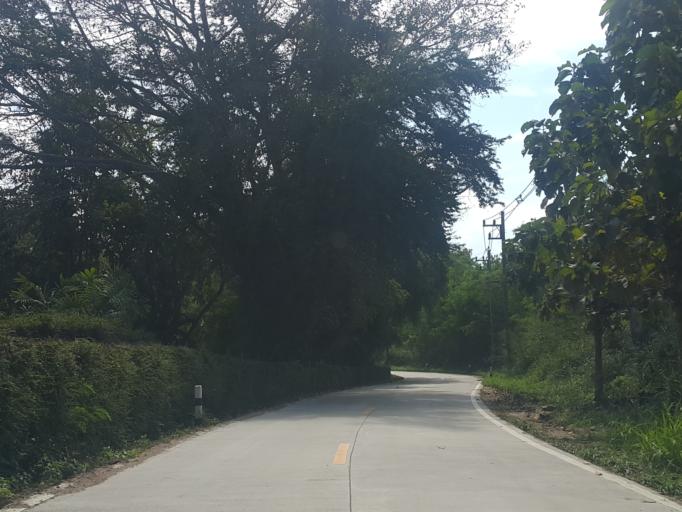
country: TH
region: Chiang Mai
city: Mae On
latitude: 18.8180
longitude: 99.2241
